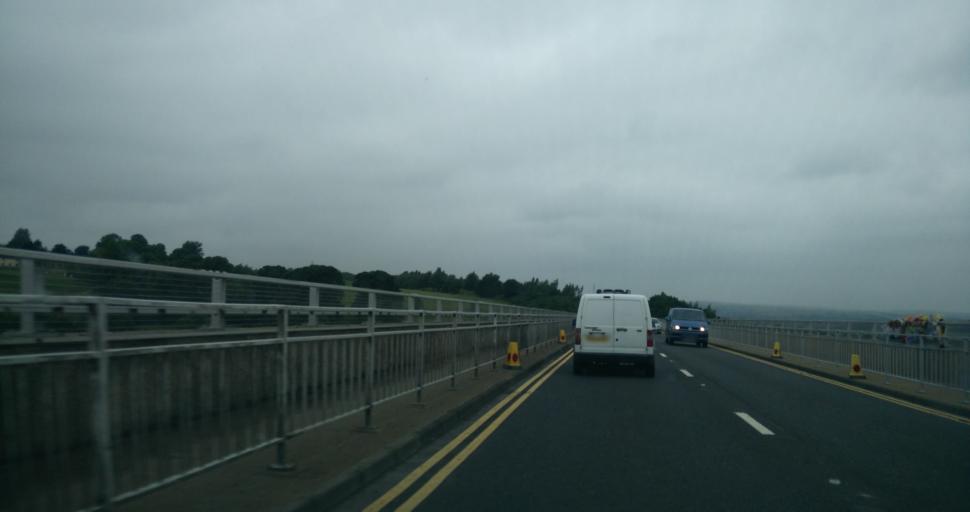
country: GB
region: England
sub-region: County Durham
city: Bishop Auckland
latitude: 54.6661
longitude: -1.6812
